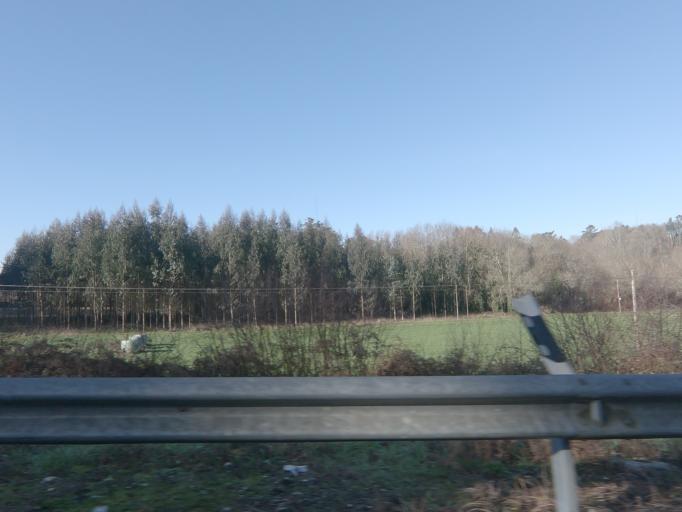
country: ES
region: Galicia
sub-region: Provincia da Coruna
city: Vedra
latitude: 42.8135
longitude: -8.4787
